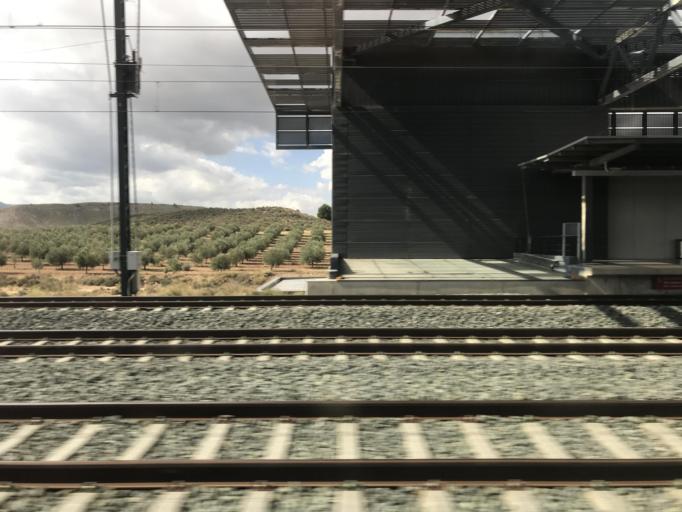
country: ES
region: Valencia
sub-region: Provincia de Alicante
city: Villena
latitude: 38.5844
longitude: -0.8739
